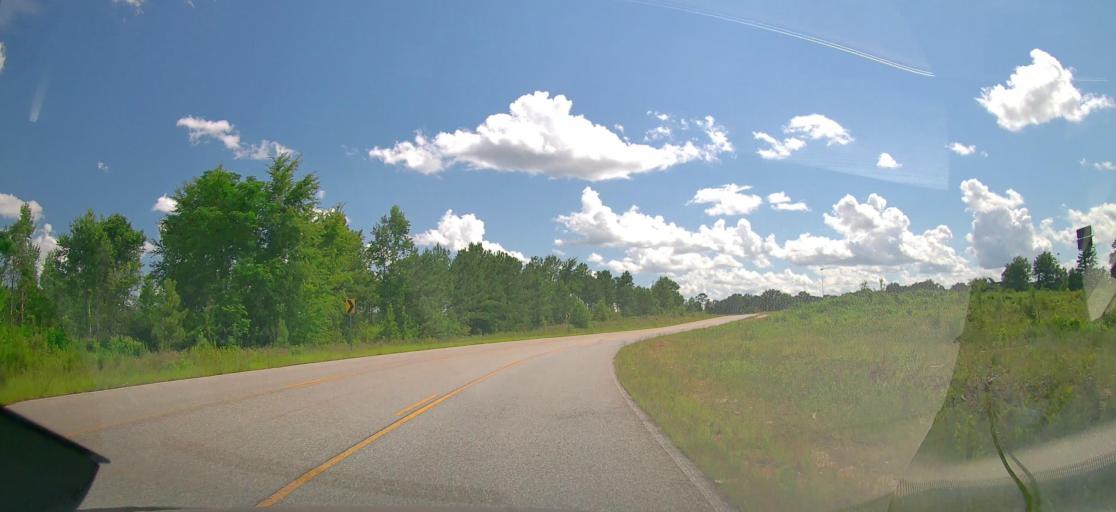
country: US
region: Georgia
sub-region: Peach County
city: Byron
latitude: 32.6117
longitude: -83.7387
